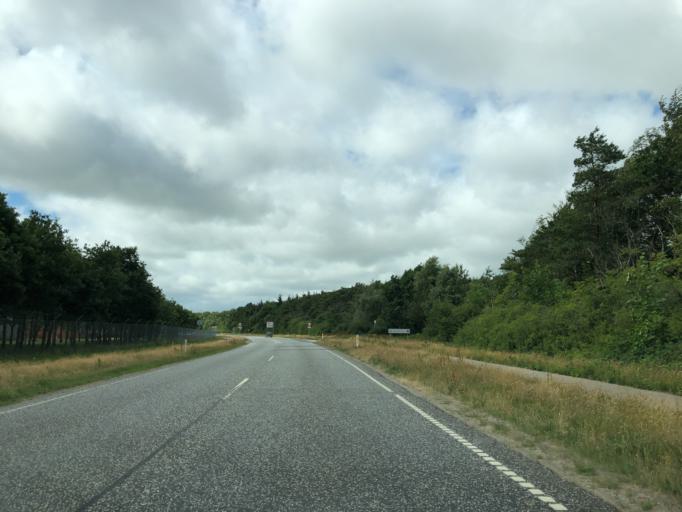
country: DK
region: Central Jutland
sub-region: Holstebro Kommune
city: Holstebro
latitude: 56.3472
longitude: 8.6076
